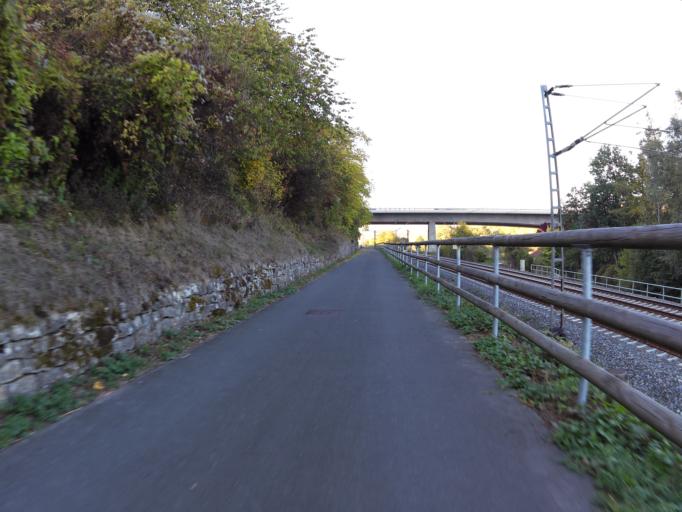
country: DE
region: Bavaria
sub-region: Regierungsbezirk Unterfranken
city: Eibelstadt
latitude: 49.7368
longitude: 9.9838
